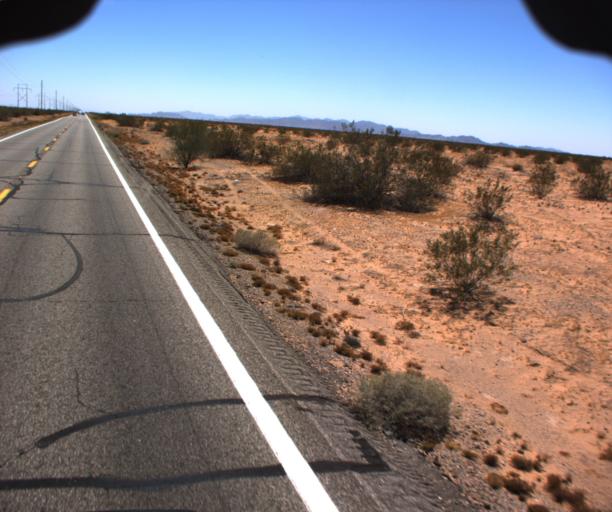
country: US
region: Arizona
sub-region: La Paz County
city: Quartzsite
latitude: 33.8884
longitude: -114.2170
